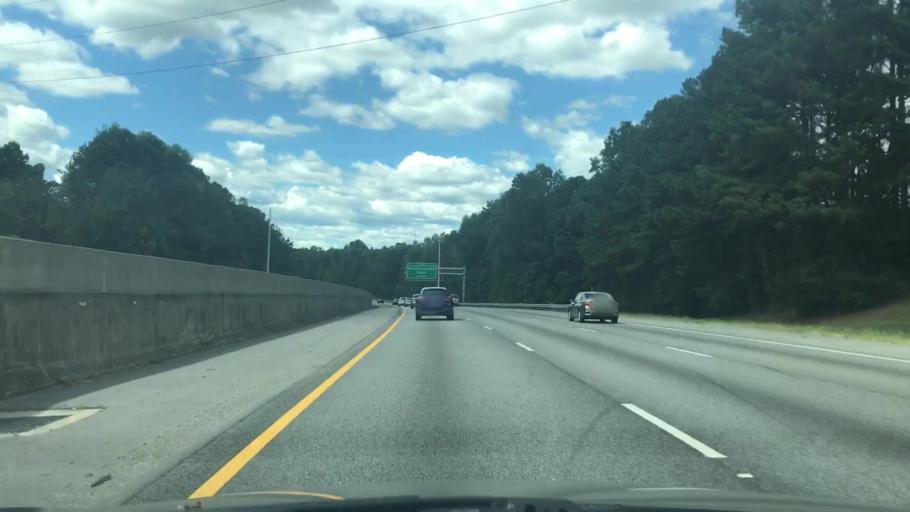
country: US
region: Georgia
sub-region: DeKalb County
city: Stone Mountain
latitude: 33.8292
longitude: -84.1786
